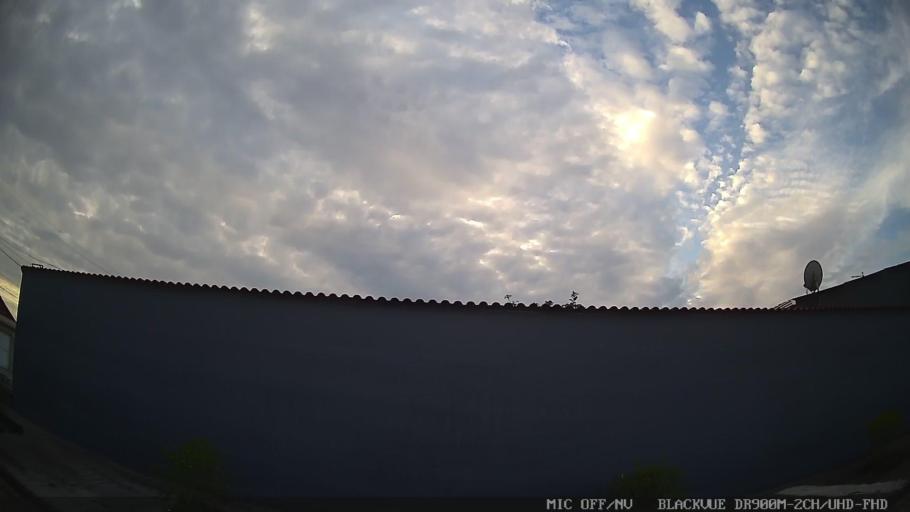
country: BR
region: Sao Paulo
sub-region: Itanhaem
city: Itanhaem
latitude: -24.1652
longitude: -46.7784
